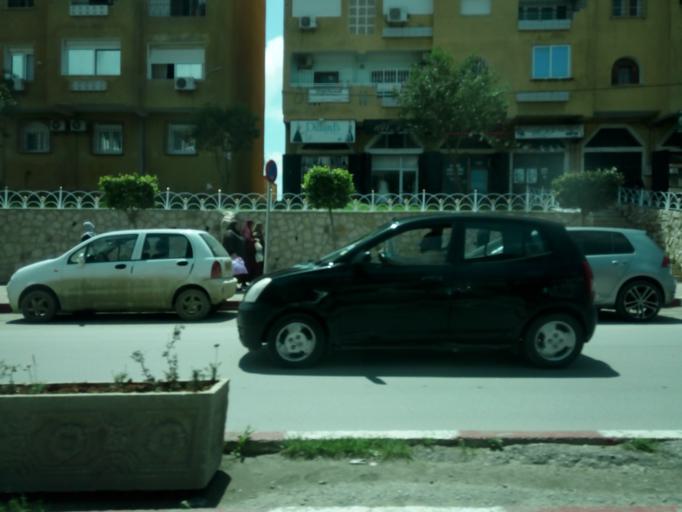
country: DZ
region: Tipaza
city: Saoula
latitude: 36.7210
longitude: 2.9939
